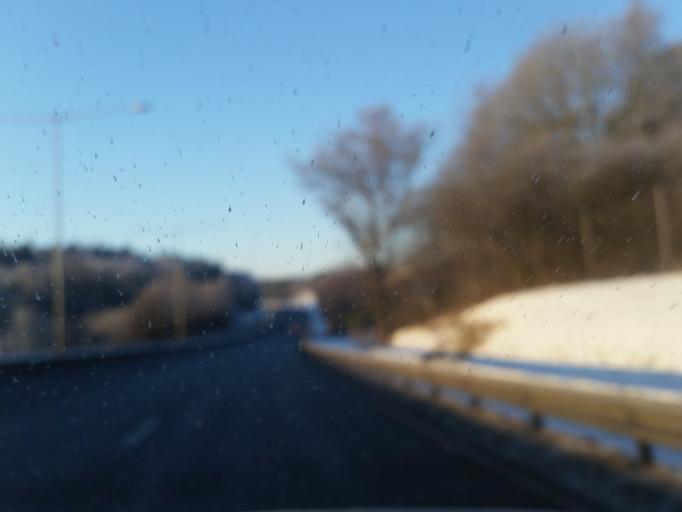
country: SE
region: Stockholm
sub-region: Botkyrka Kommun
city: Eriksberg
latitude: 59.2308
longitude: 17.8011
